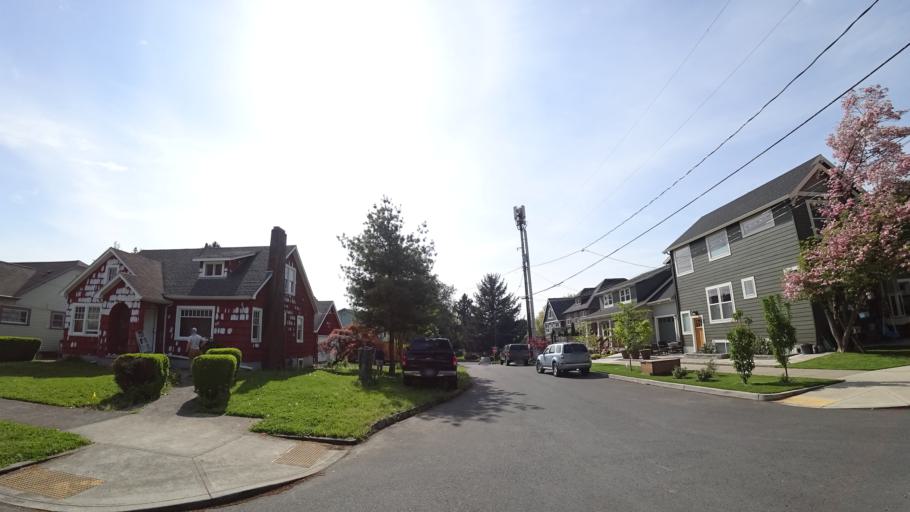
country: US
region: Oregon
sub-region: Clackamas County
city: Milwaukie
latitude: 45.4785
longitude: -122.6217
